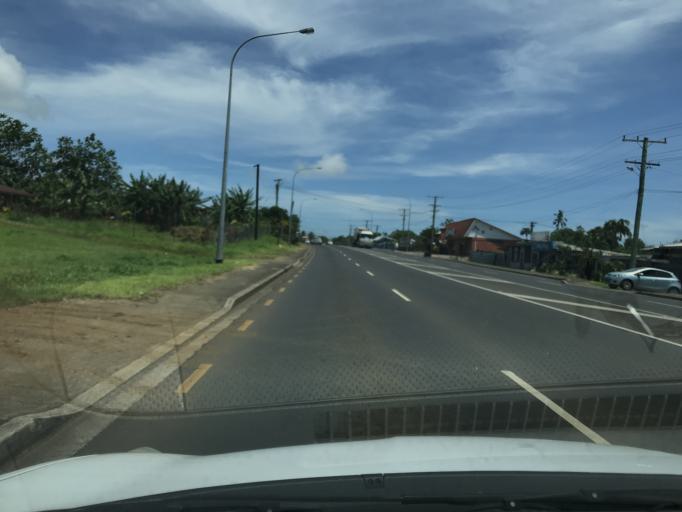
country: WS
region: Tuamasaga
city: Vaiusu
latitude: -13.8259
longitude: -171.7945
